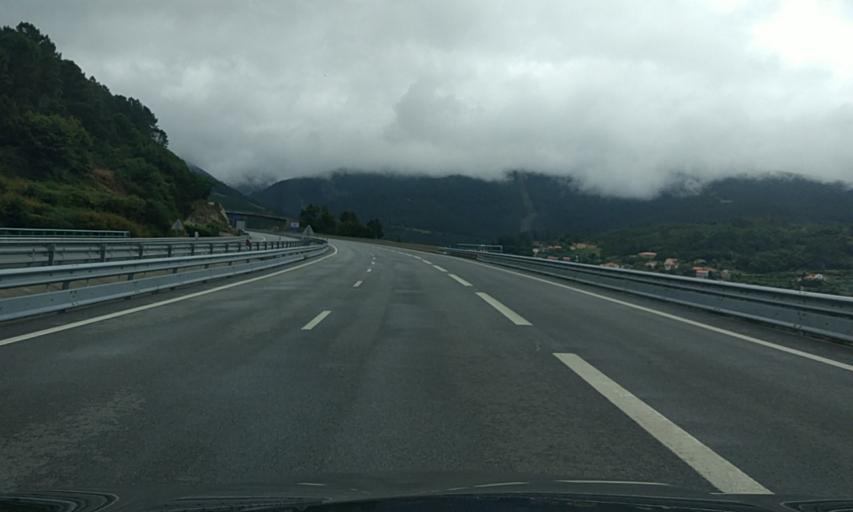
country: PT
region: Porto
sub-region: Baiao
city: Valadares
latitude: 41.2551
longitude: -7.9627
